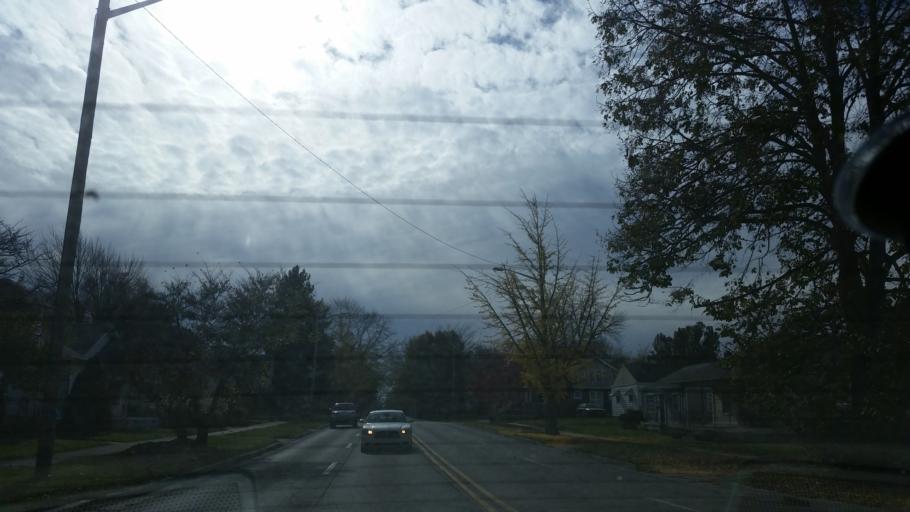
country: US
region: Indiana
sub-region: Howard County
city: Kokomo
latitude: 40.4739
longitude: -86.1338
